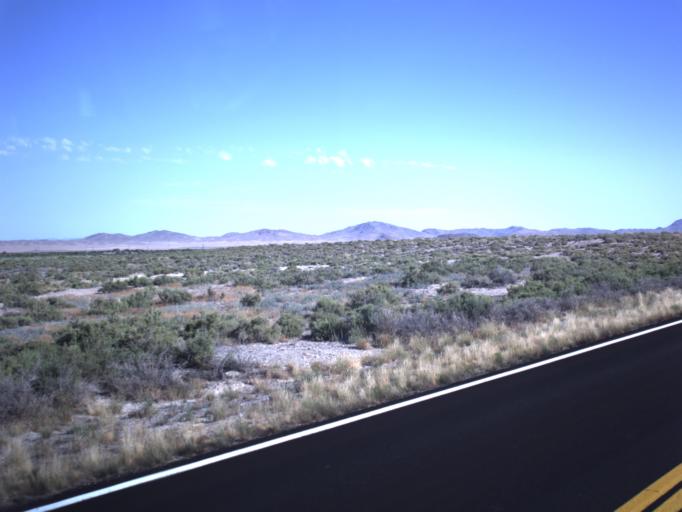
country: US
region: Utah
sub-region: Beaver County
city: Milford
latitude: 38.6235
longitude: -112.9849
